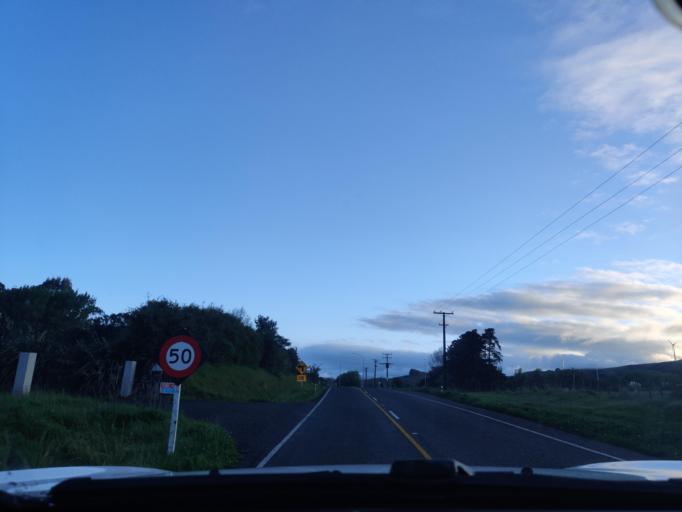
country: NZ
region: Manawatu-Wanganui
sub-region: Palmerston North City
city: Palmerston North
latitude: -40.3107
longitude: 175.7611
